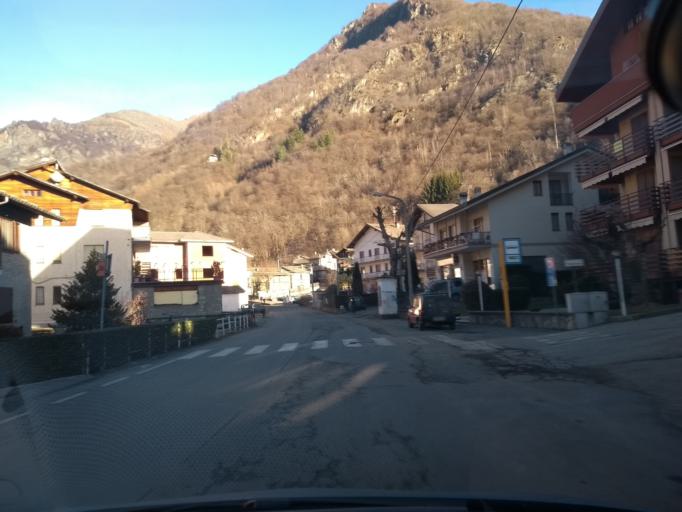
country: IT
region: Piedmont
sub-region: Provincia di Torino
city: Cantoira
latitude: 45.3376
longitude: 7.3870
